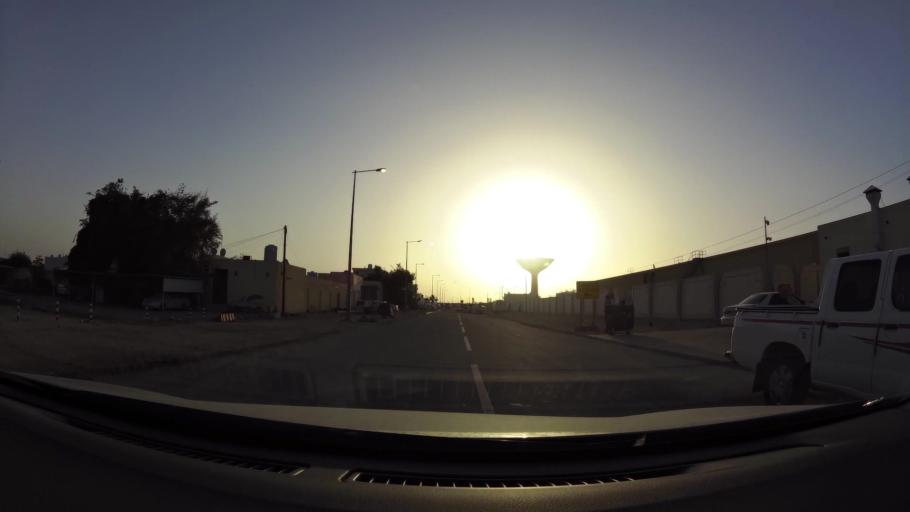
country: QA
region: Baladiyat ar Rayyan
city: Ar Rayyan
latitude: 25.3151
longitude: 51.4541
